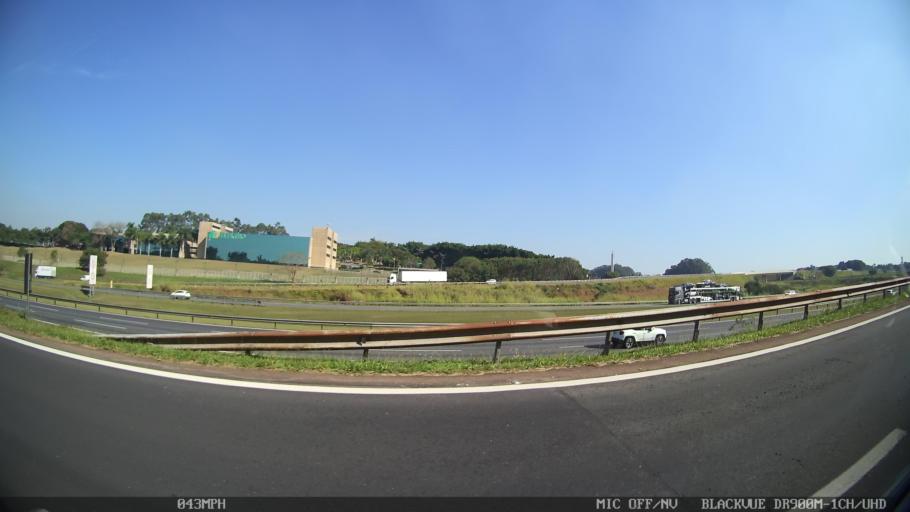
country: BR
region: Sao Paulo
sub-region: Campinas
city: Campinas
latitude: -22.9955
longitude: -47.1053
